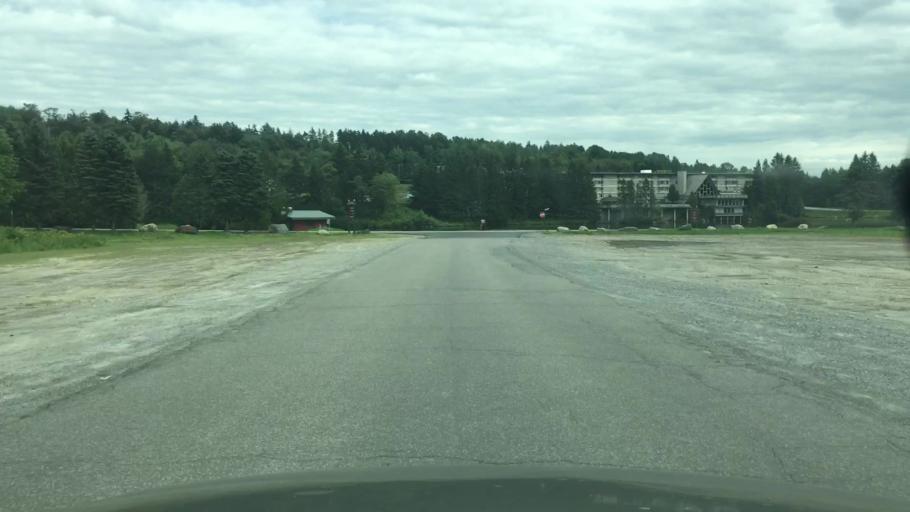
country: US
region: Vermont
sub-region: Windham County
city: Dover
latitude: 42.9668
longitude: -72.8909
